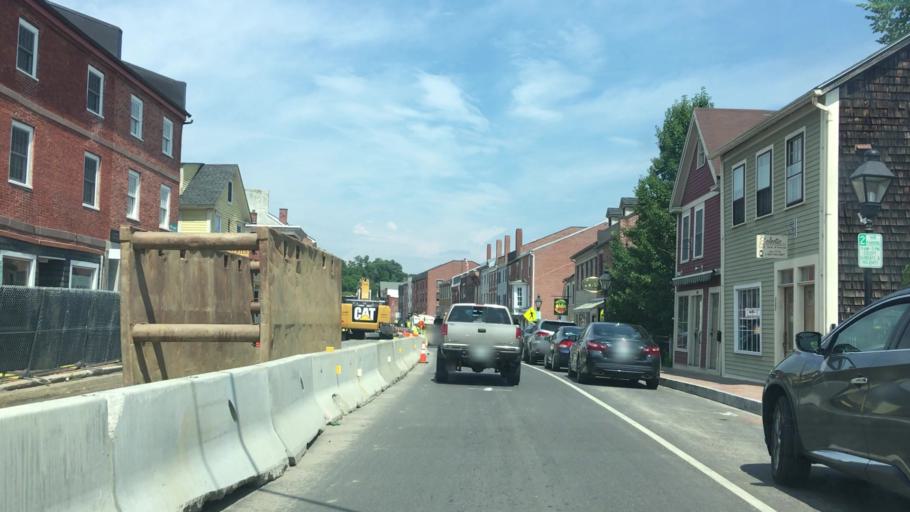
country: US
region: Maine
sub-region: Kennebec County
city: Hallowell
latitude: 44.2846
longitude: -69.7905
